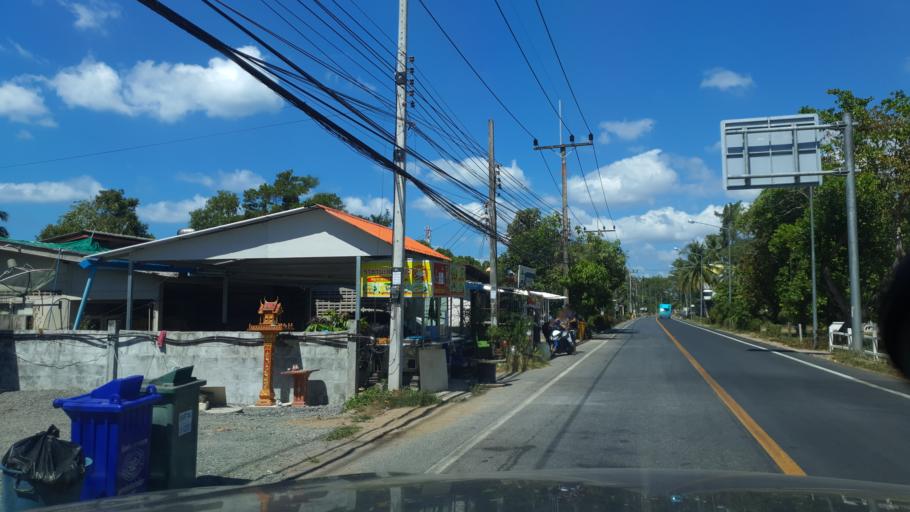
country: TH
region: Phuket
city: Thalang
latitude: 8.1363
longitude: 98.3068
